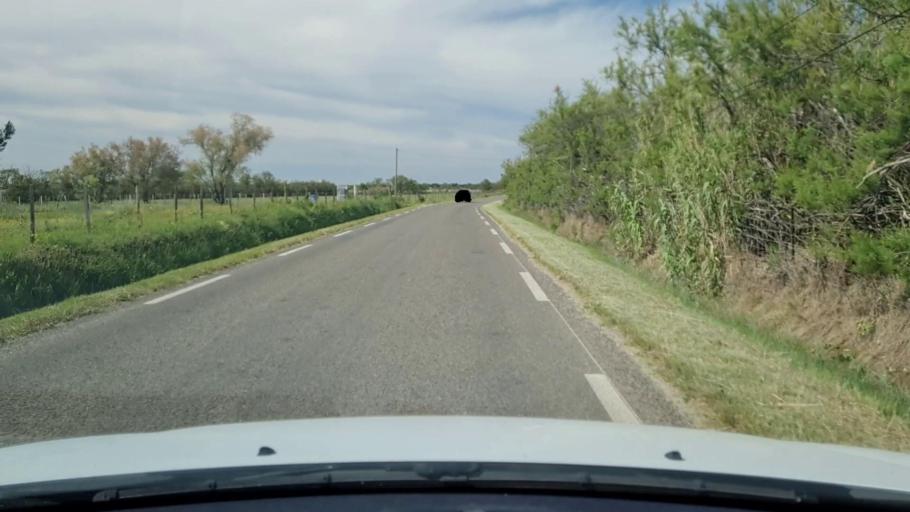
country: FR
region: Languedoc-Roussillon
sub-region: Departement du Gard
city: Aigues-Mortes
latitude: 43.6014
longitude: 4.2112
